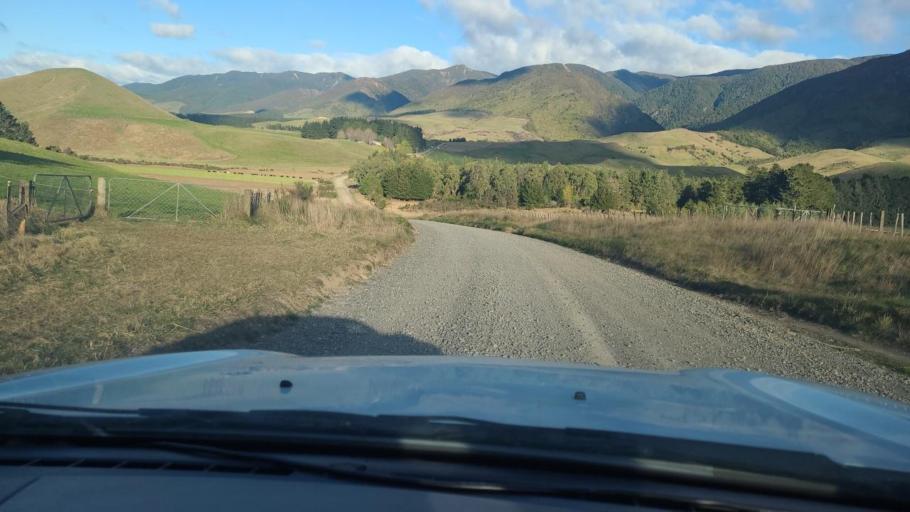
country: NZ
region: Hawke's Bay
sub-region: Hastings District
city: Hastings
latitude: -39.6352
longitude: 176.3346
